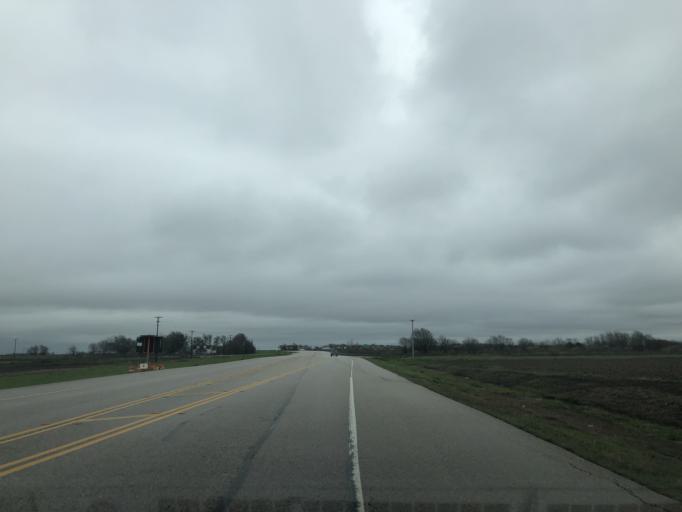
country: US
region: Texas
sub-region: Williamson County
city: Hutto
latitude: 30.6022
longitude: -97.5075
